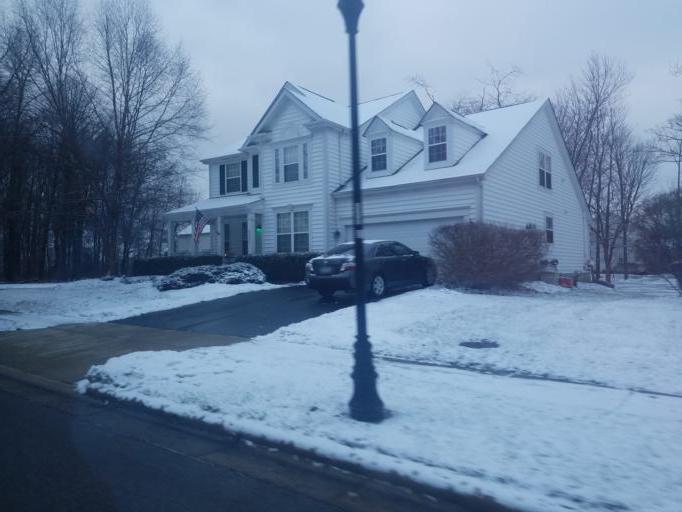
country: US
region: Ohio
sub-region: Franklin County
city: New Albany
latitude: 40.0683
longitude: -82.8493
